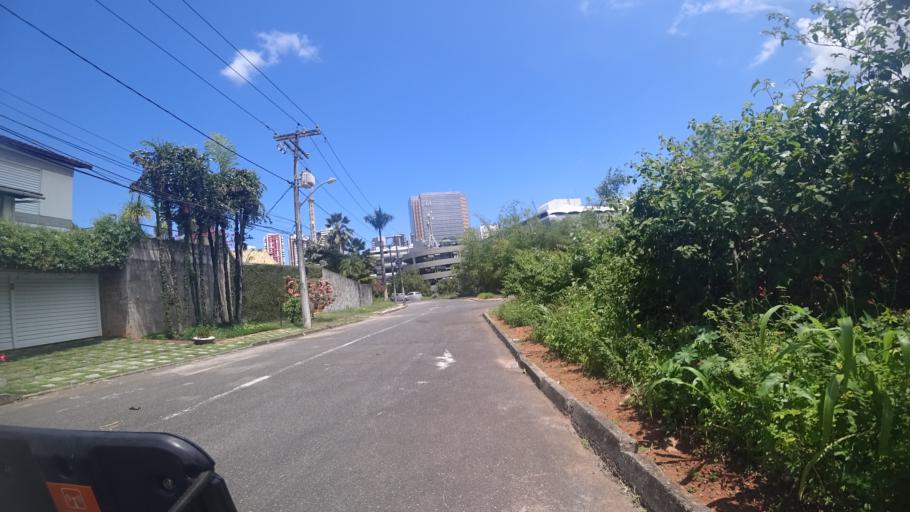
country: BR
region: Bahia
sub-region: Salvador
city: Salvador
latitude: -12.9945
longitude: -38.4667
